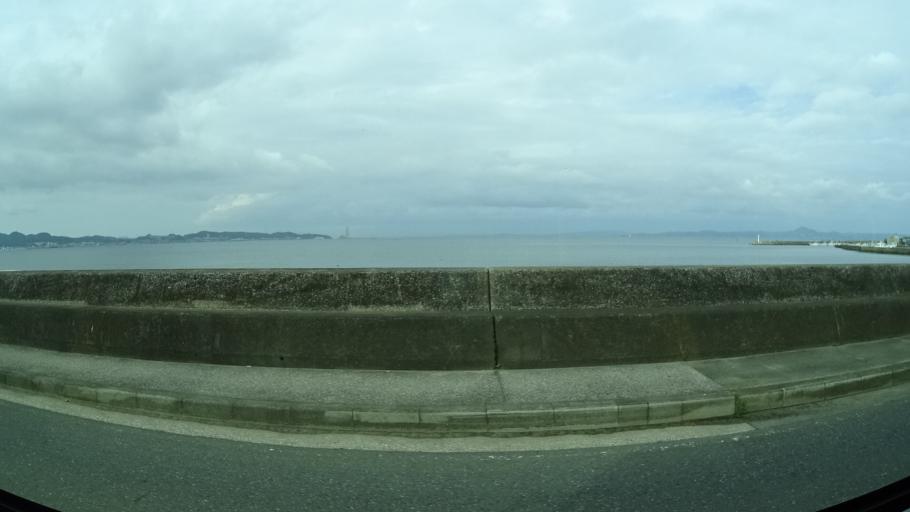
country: JP
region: Kanagawa
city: Miura
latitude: 35.1603
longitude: 139.6619
